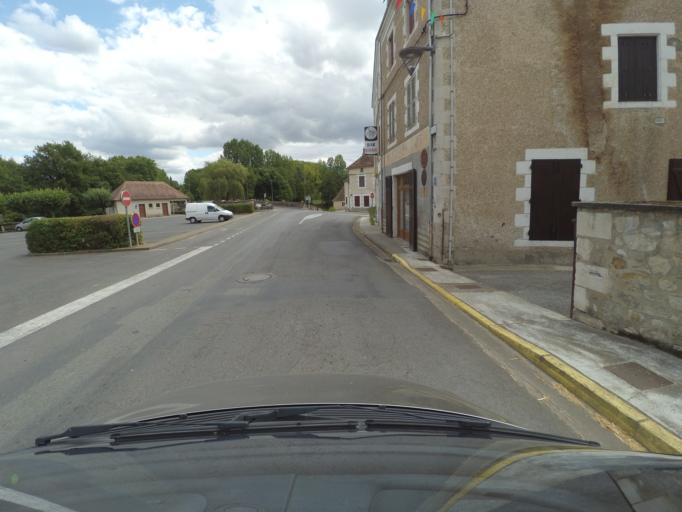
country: FR
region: Centre
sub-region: Departement de l'Indre
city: Belabre
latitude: 46.4669
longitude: 1.0422
